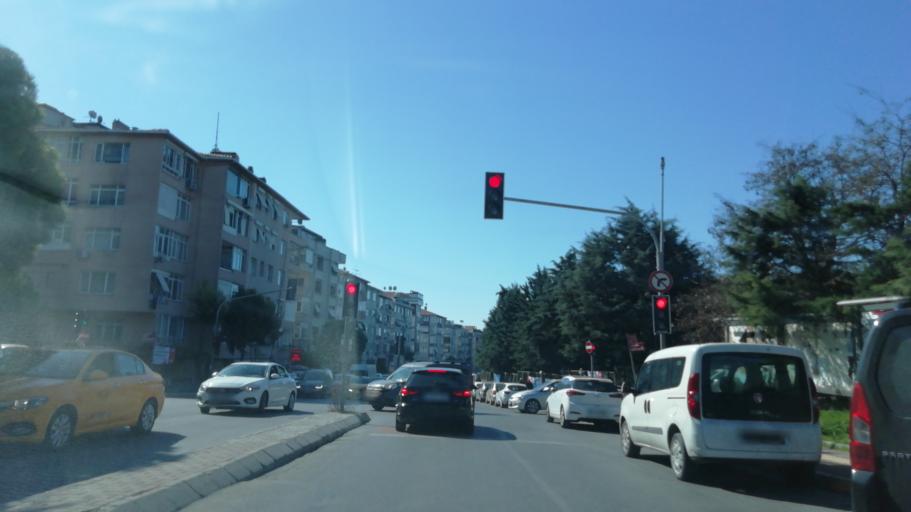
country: TR
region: Istanbul
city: Bahcelievler
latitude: 40.9931
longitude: 28.8674
